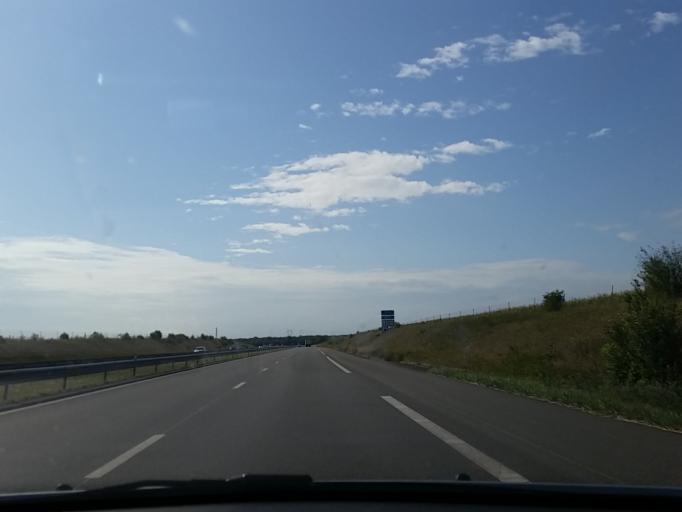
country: FR
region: Centre
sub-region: Departement du Cher
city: Plaimpied-Givaudins
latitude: 46.9950
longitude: 2.4071
